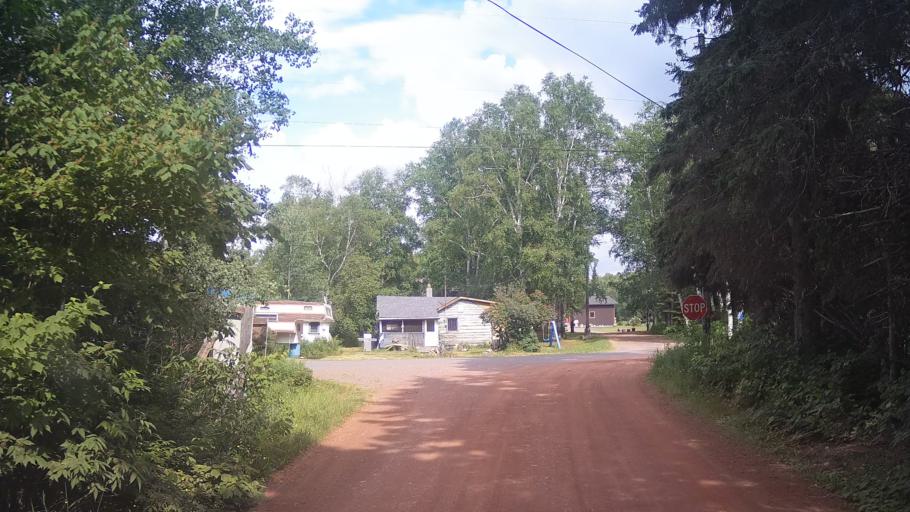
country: CA
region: Ontario
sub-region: Thunder Bay District
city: Thunder Bay
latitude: 48.6655
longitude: -88.6624
